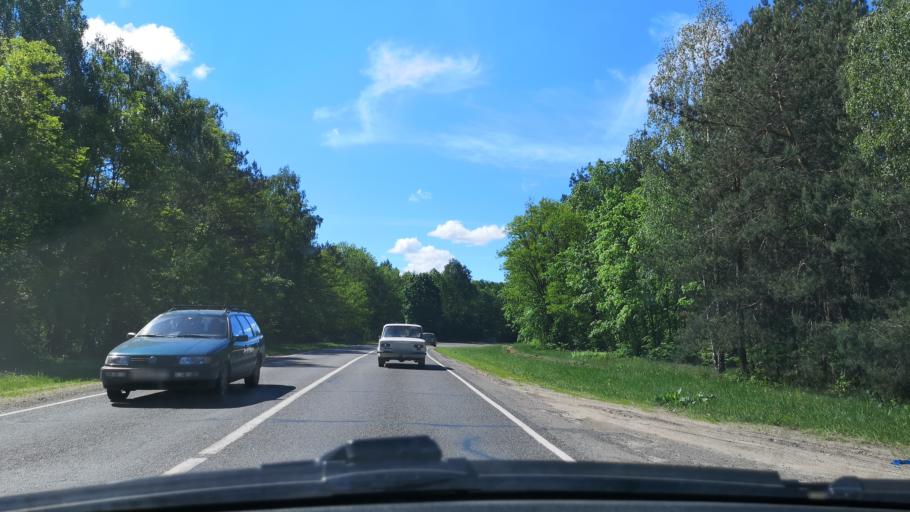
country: BY
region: Brest
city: Brest
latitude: 52.0230
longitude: 23.7302
